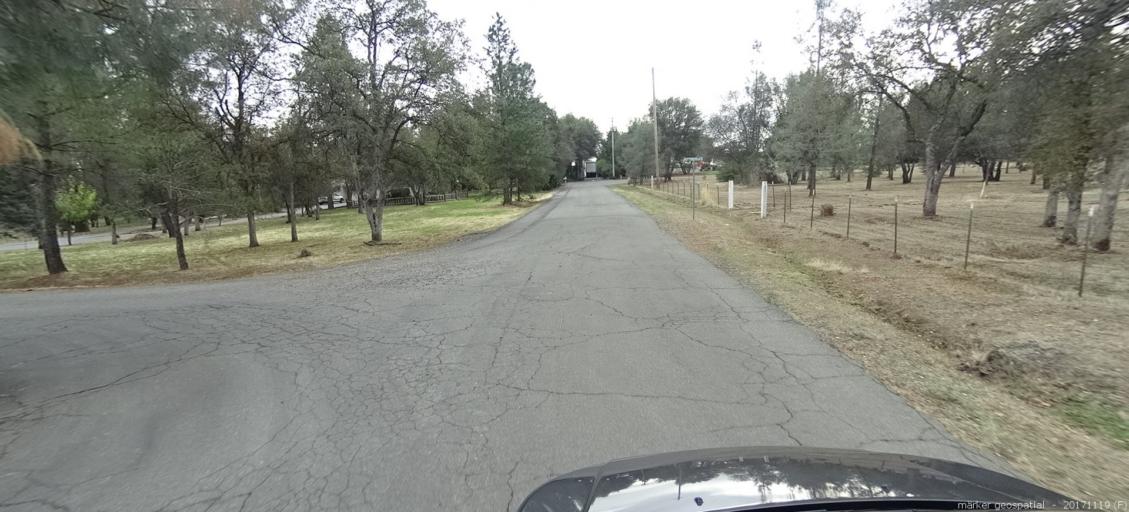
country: US
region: California
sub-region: Shasta County
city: Shasta
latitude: 40.4791
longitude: -122.4641
